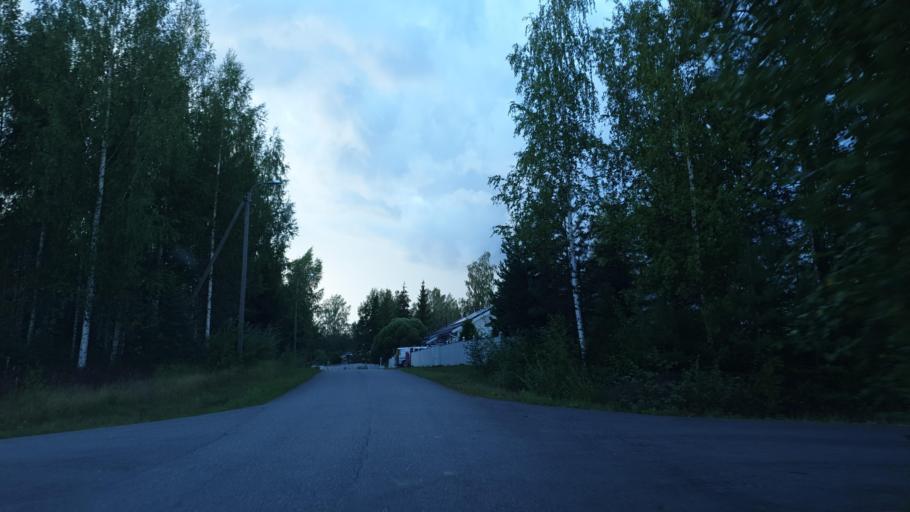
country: FI
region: Northern Savo
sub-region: Varkaus
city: Leppaevirta
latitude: 62.5831
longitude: 27.6215
